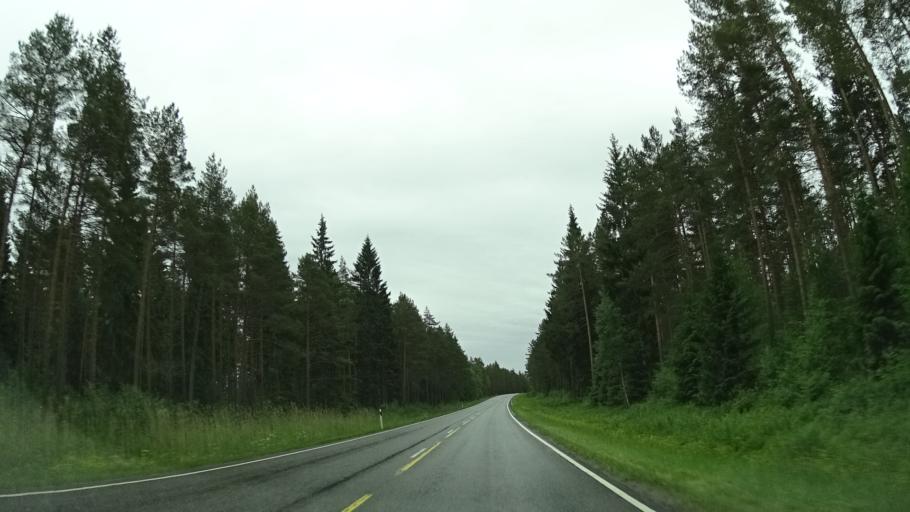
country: FI
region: Varsinais-Suomi
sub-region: Salo
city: Pernioe
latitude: 60.1130
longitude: 23.2126
